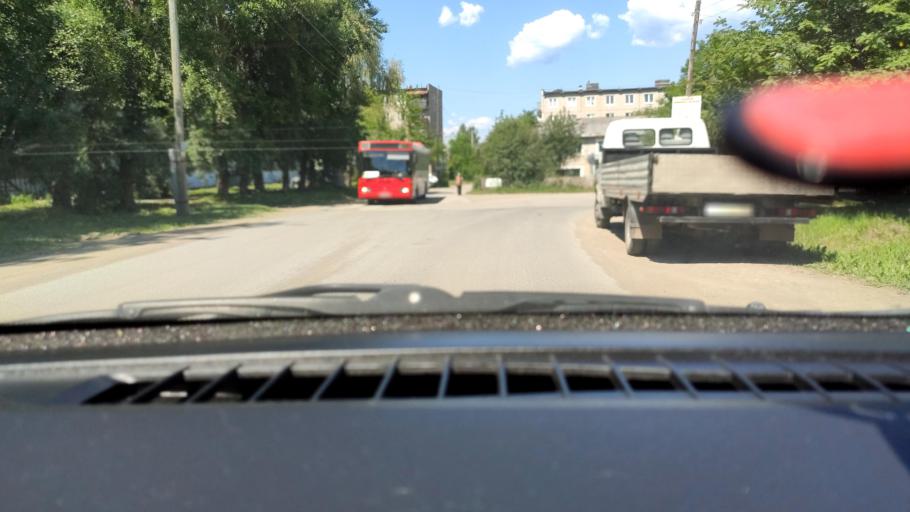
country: RU
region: Perm
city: Sylva
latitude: 58.0309
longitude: 56.7457
